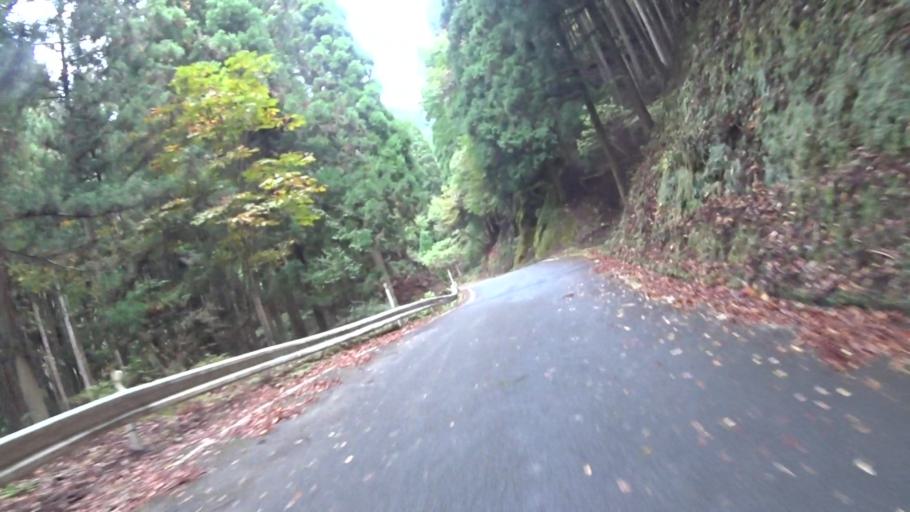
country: JP
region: Fukui
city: Obama
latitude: 35.2780
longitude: 135.7197
